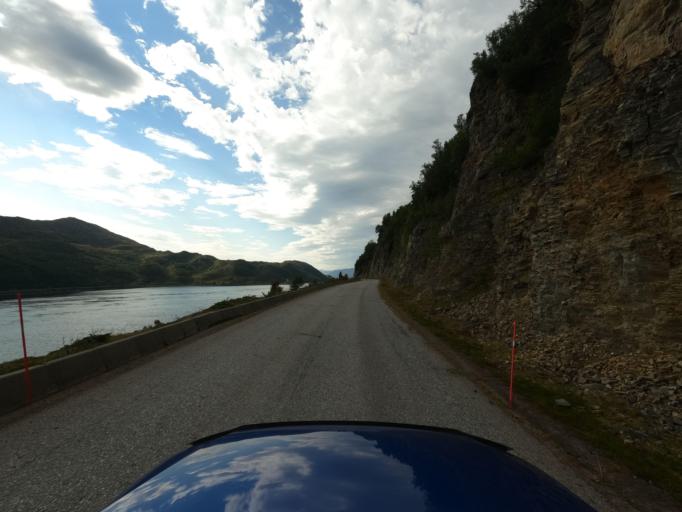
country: NO
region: Finnmark Fylke
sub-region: Kvalsund
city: Kvalsund
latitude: 70.5110
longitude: 23.9209
